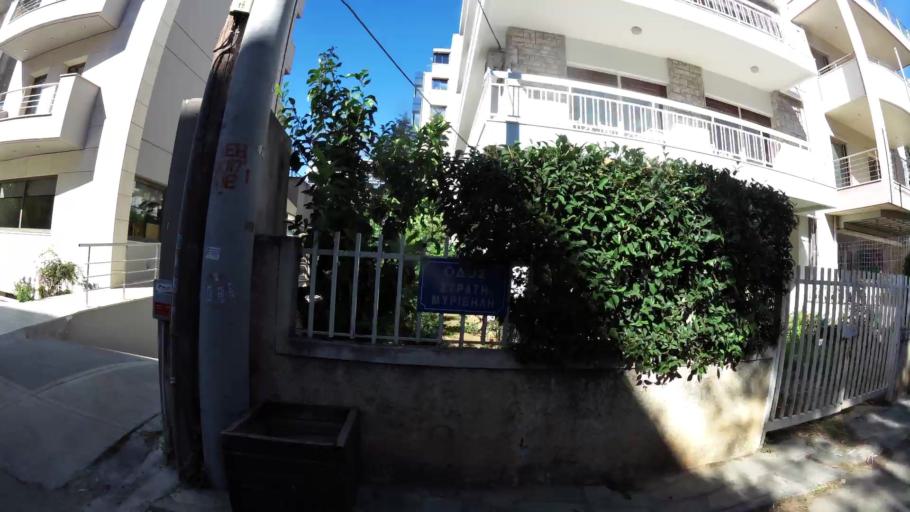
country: GR
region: Attica
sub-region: Nomarchia Athinas
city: Filothei
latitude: 38.0278
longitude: 23.7916
